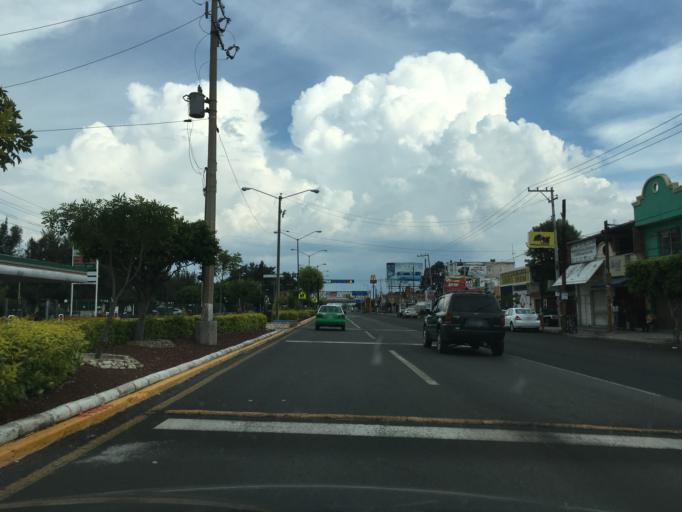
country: MX
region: Guanajuato
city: Celaya
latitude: 20.5401
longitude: -100.8203
